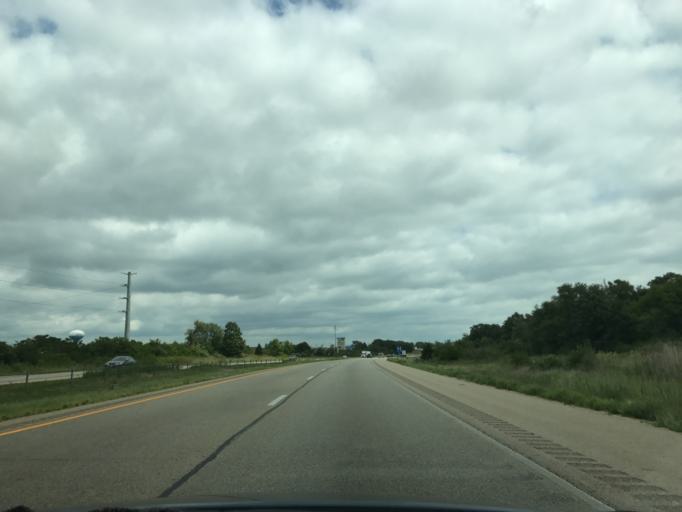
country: US
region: Illinois
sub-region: LaSalle County
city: Ottawa
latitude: 41.3733
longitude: -88.8476
